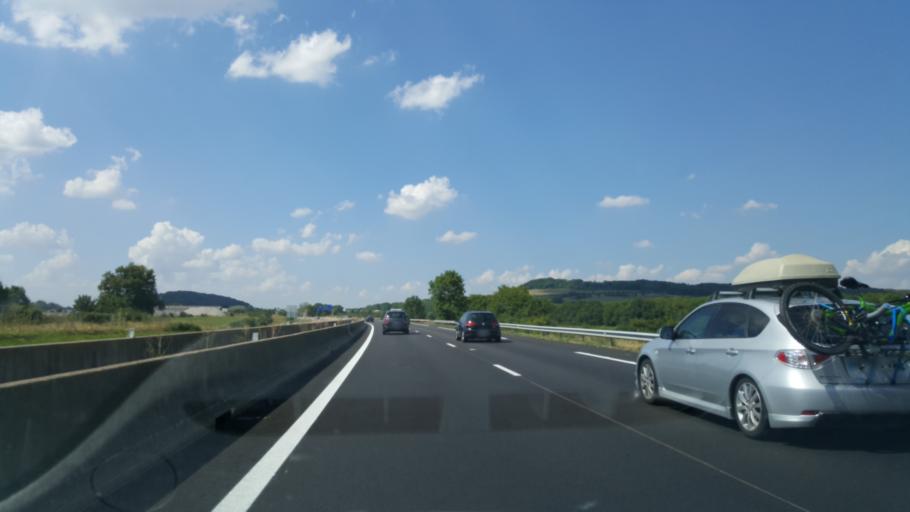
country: FR
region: Bourgogne
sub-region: Departement de la Cote-d'Or
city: Pouilly-en-Auxois
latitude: 47.2428
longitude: 4.5768
